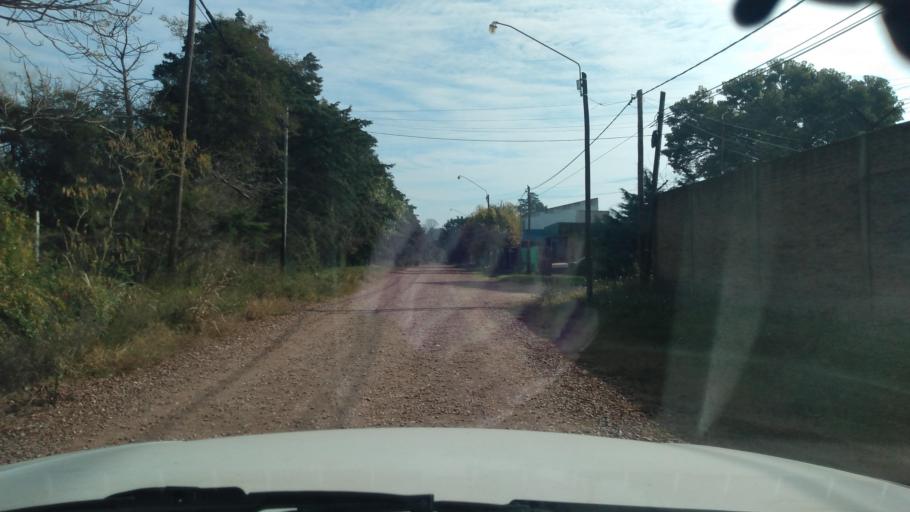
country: AR
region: Buenos Aires
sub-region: Partido de Lujan
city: Lujan
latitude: -34.5892
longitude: -59.1254
